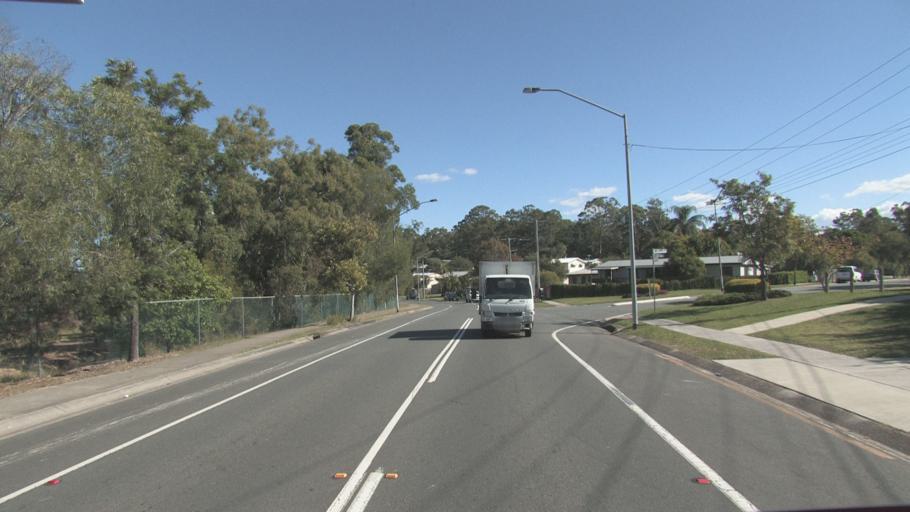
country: AU
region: Queensland
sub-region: Logan
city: Woodridge
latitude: -27.6281
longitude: 153.0982
